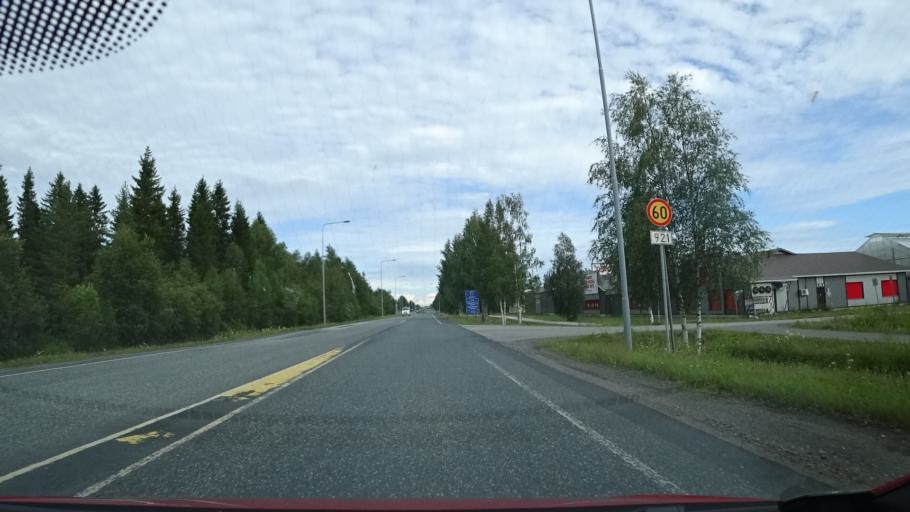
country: FI
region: Lapland
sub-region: Kemi-Tornio
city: Keminmaa
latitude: 65.8016
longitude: 24.4922
